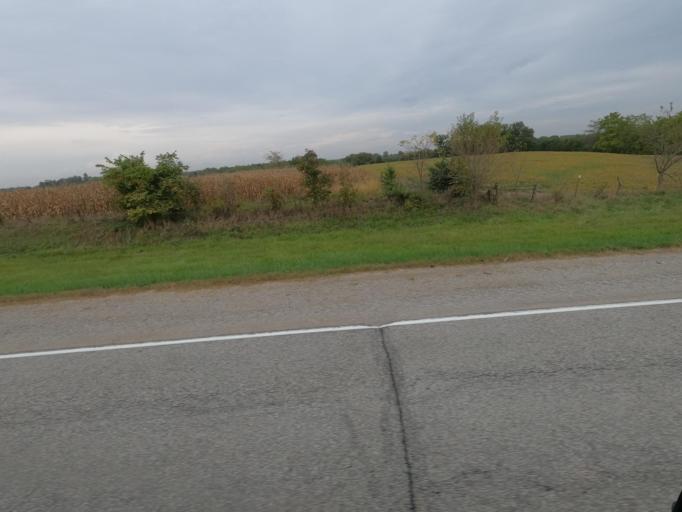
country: US
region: Iowa
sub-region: Van Buren County
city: Keosauqua
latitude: 40.8509
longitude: -92.0495
